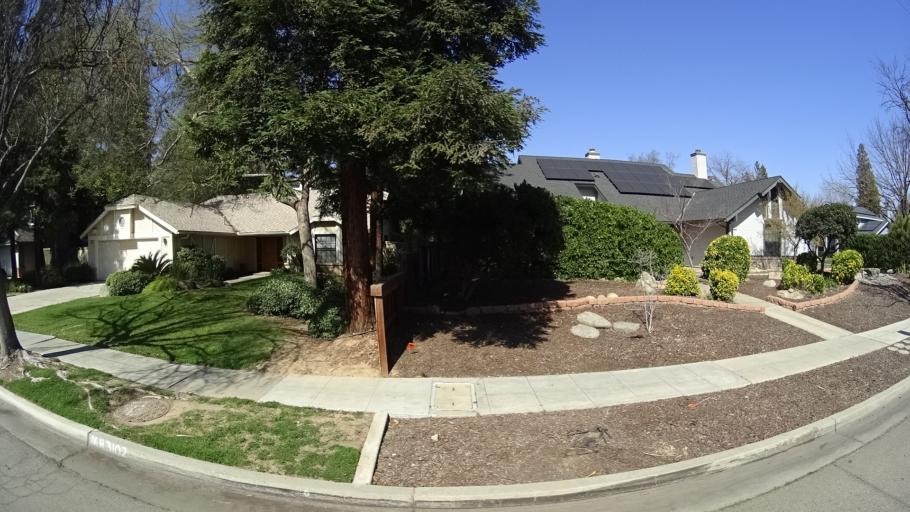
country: US
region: California
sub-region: Fresno County
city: Fresno
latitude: 36.8301
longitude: -119.8122
